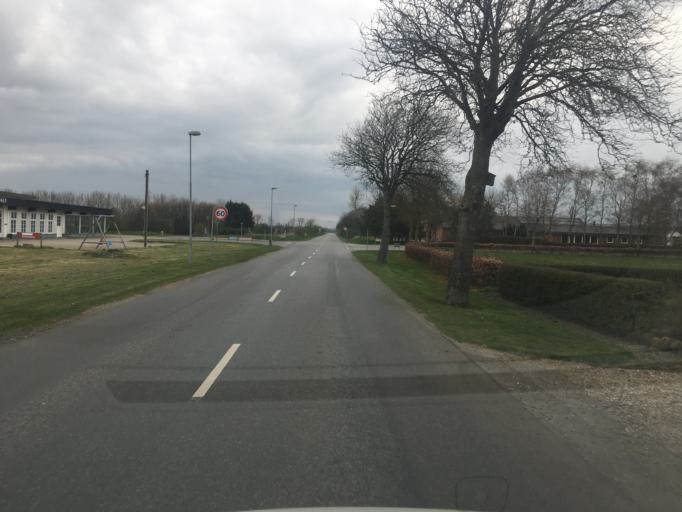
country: DK
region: South Denmark
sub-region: Tonder Kommune
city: Toftlund
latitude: 55.0634
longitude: 9.0989
